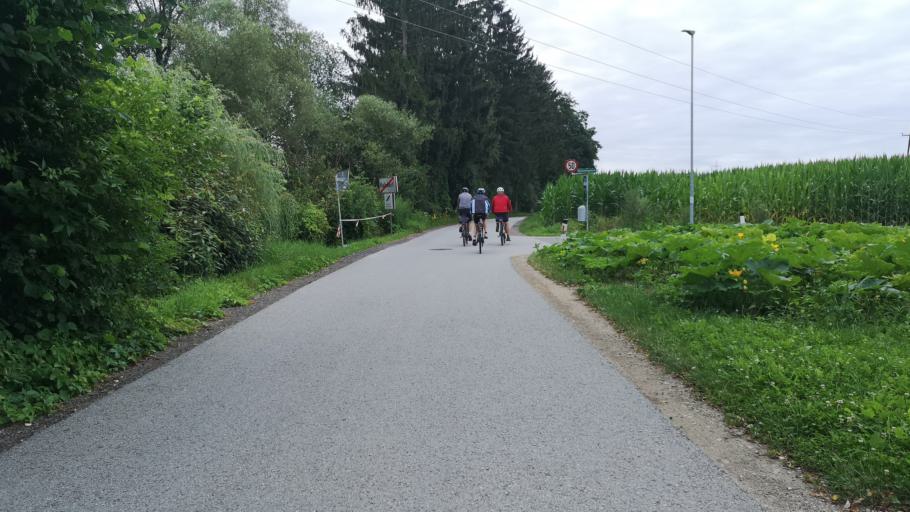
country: AT
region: Styria
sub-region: Politischer Bezirk Graz-Umgebung
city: Kalsdorf bei Graz
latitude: 46.9539
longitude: 15.4879
